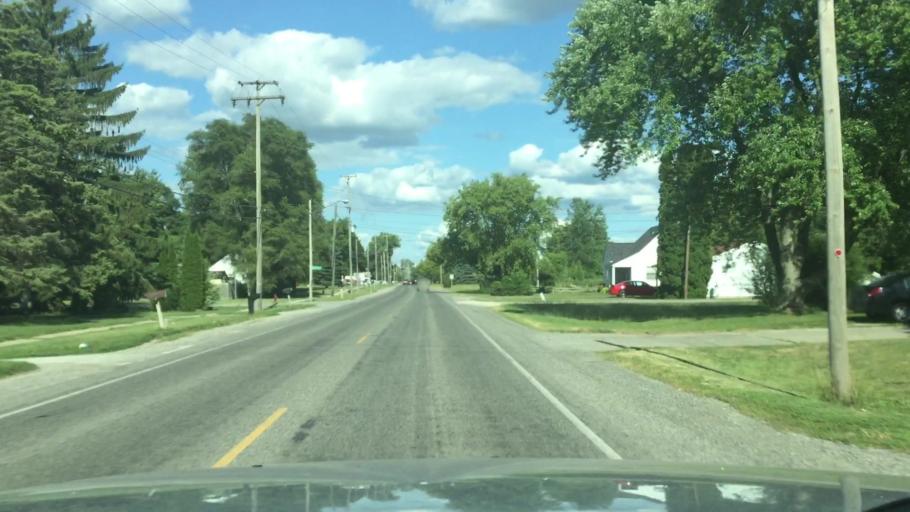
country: US
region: Michigan
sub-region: Saginaw County
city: Saginaw
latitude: 43.4008
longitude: -84.0018
